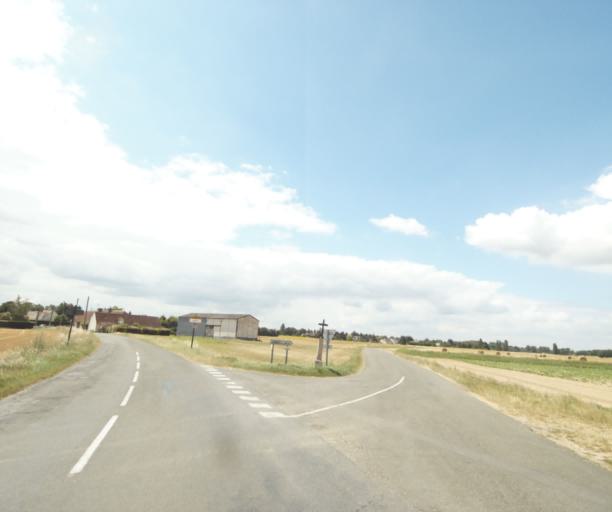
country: FR
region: Centre
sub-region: Departement du Loiret
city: Mardie
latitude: 47.8800
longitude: 2.0509
